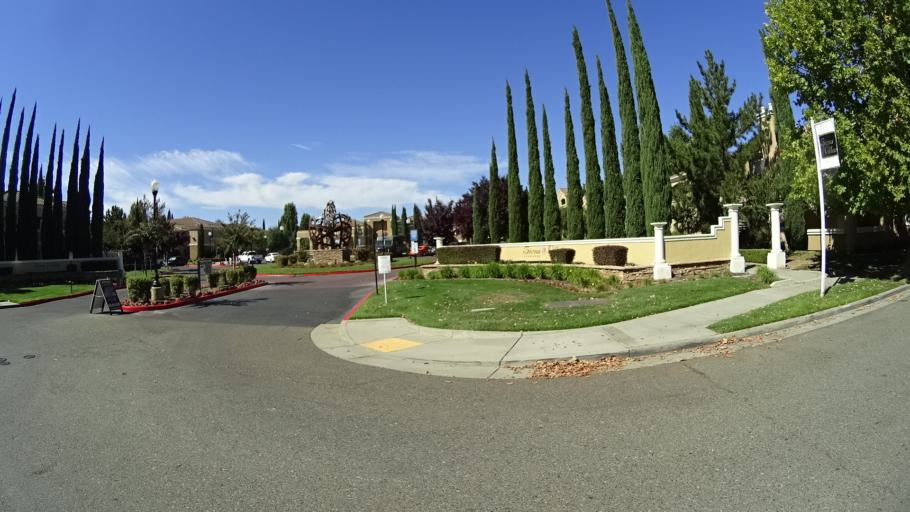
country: US
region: California
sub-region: Sacramento County
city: Laguna
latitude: 38.4255
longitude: -121.4715
